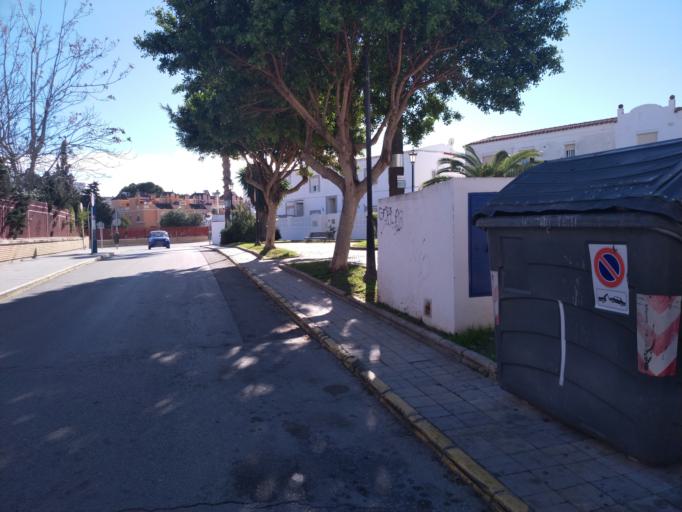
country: ES
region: Andalusia
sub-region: Provincia de Cadiz
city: San Fernando
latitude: 36.4792
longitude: -6.1957
